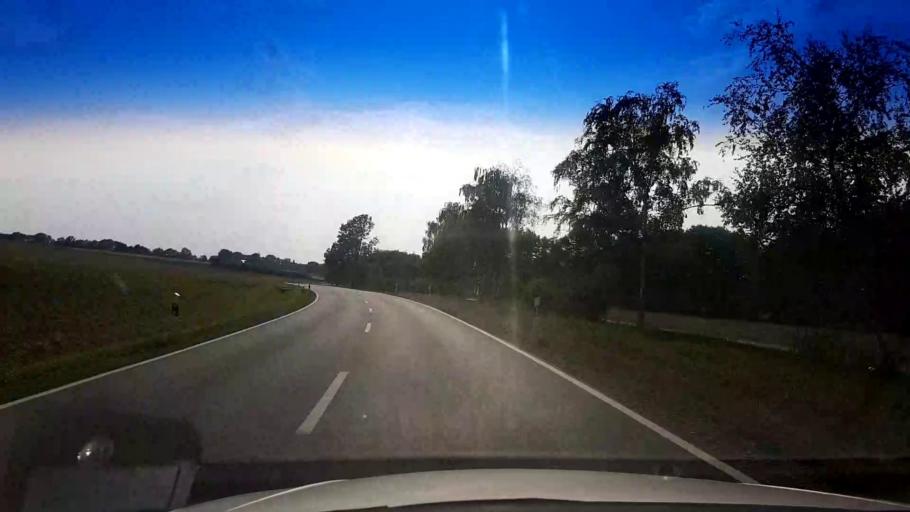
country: DE
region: Bavaria
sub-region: Upper Franconia
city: Schesslitz
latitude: 49.9650
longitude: 11.0130
